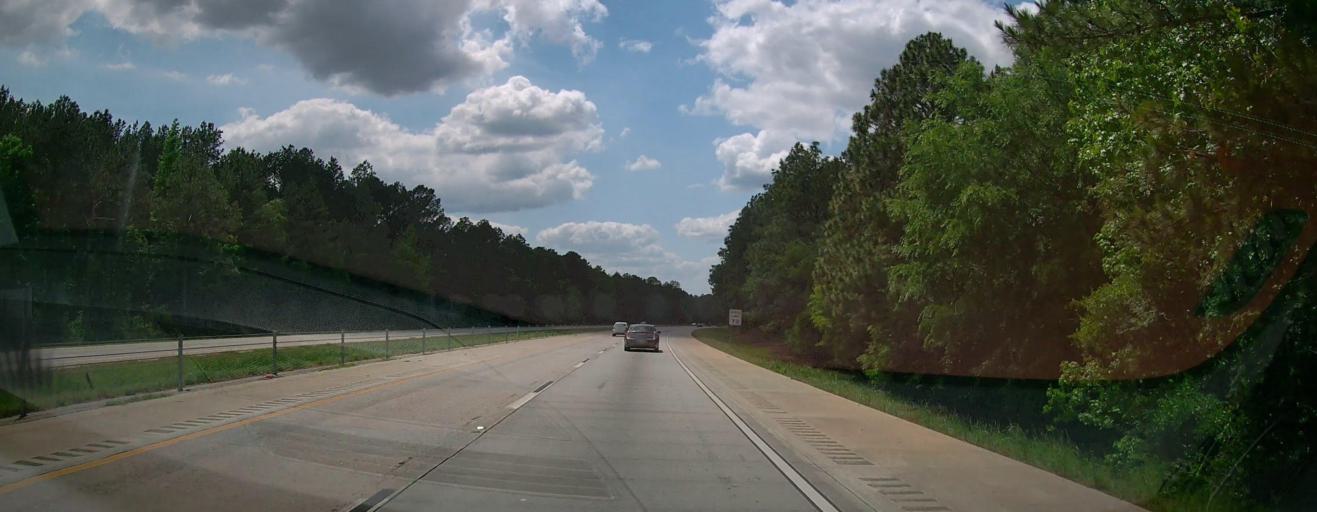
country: US
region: Georgia
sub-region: Treutlen County
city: Soperton
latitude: 32.4342
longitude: -82.6914
